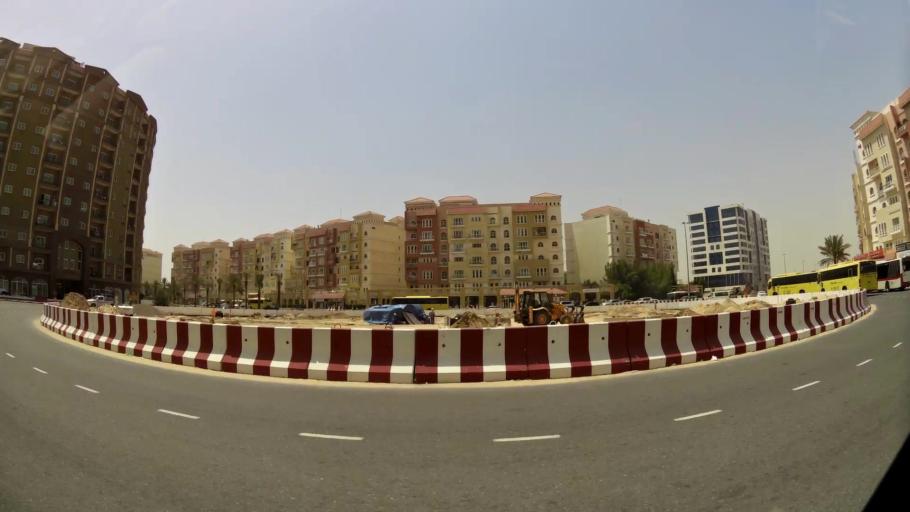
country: AE
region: Ash Shariqah
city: Sharjah
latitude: 25.1685
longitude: 55.4093
